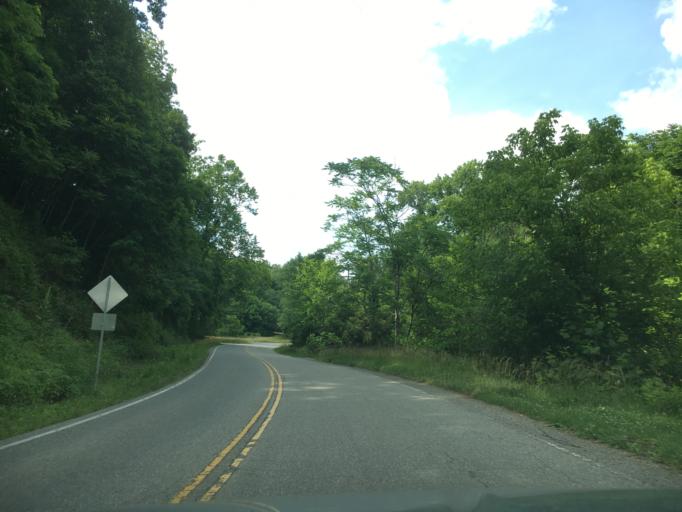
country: US
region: Virginia
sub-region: Roanoke County
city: Narrows
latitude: 37.1808
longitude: -80.0006
